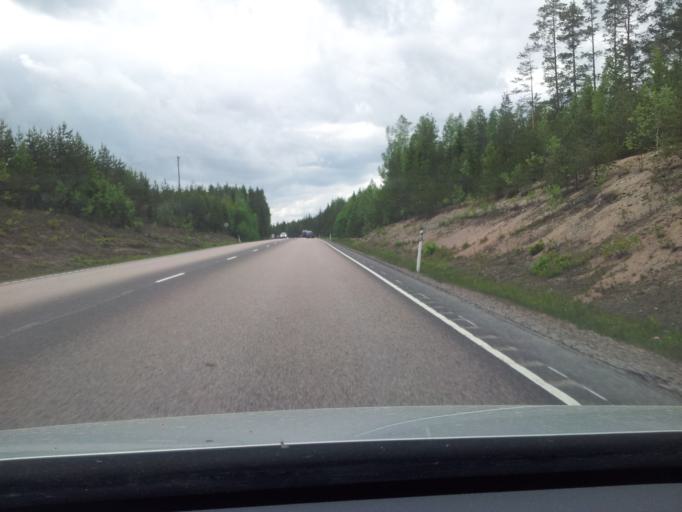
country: FI
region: South Karelia
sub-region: Lappeenranta
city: Taavetti
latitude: 60.9167
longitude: 27.4346
